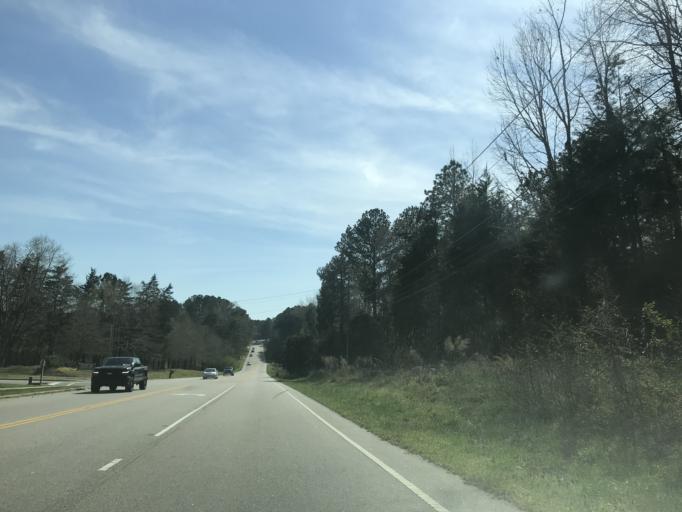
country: US
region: North Carolina
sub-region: Wake County
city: Knightdale
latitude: 35.8414
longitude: -78.5418
